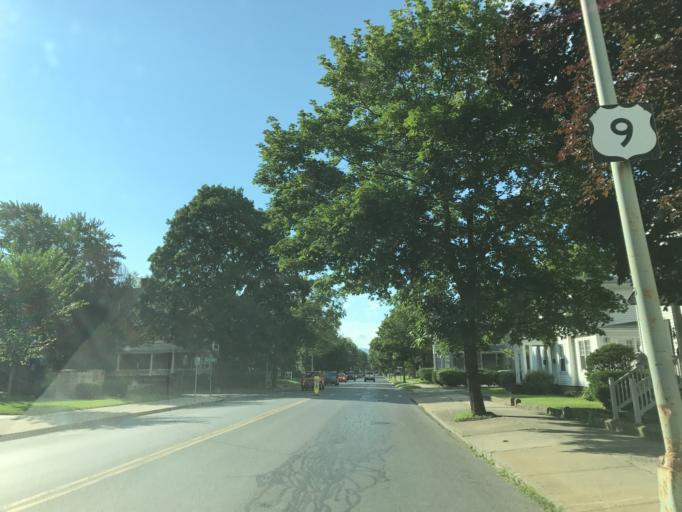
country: US
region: New York
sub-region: Warren County
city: Glens Falls
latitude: 43.3125
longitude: -73.6502
